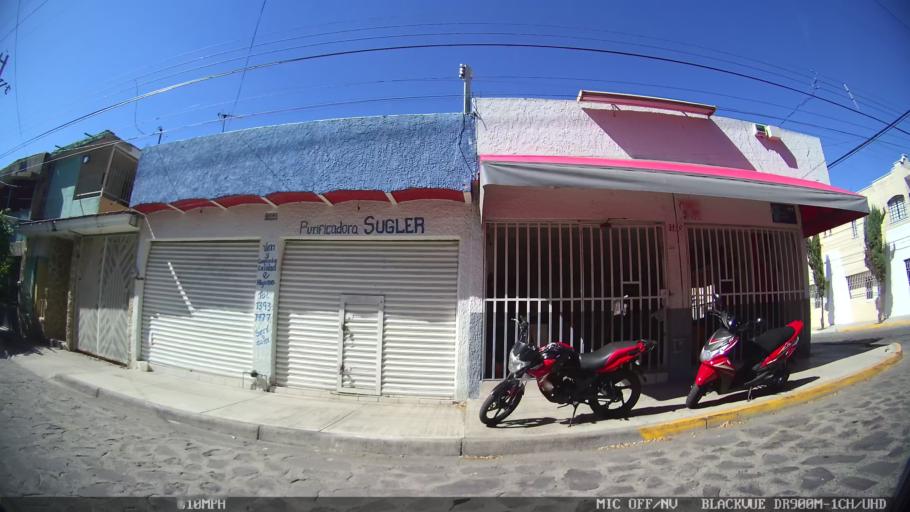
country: MX
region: Jalisco
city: Tlaquepaque
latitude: 20.6816
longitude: -103.2770
